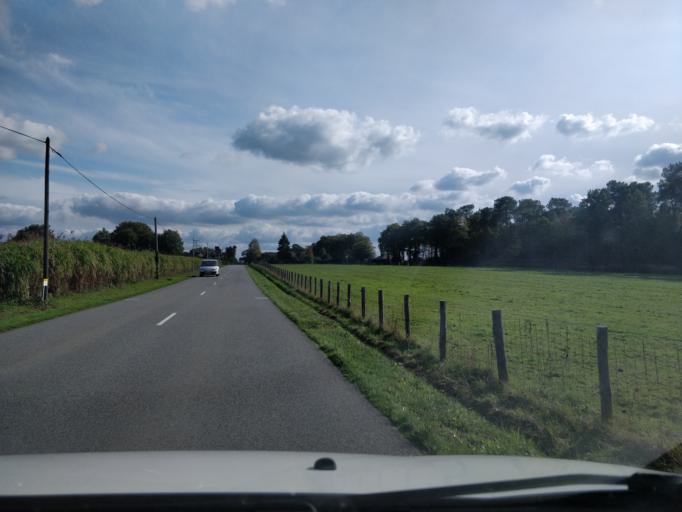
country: FR
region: Brittany
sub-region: Departement d'Ille-et-Vilaine
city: La Bouexiere
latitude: 48.1618
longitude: -1.4183
